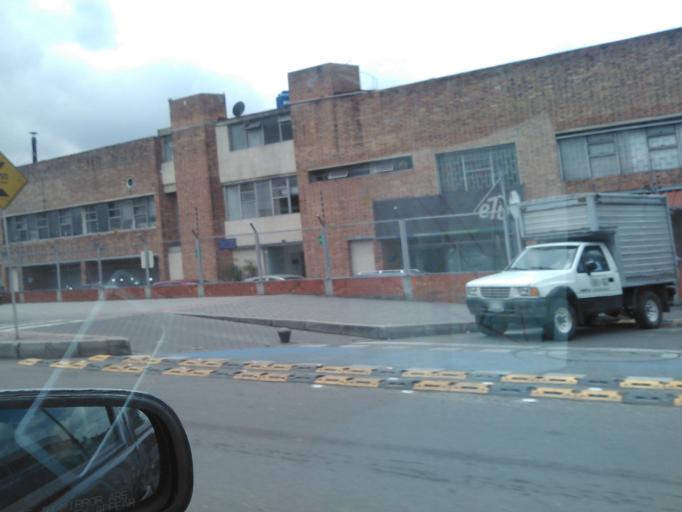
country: CO
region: Bogota D.C.
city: Bogota
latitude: 4.6279
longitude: -74.1153
